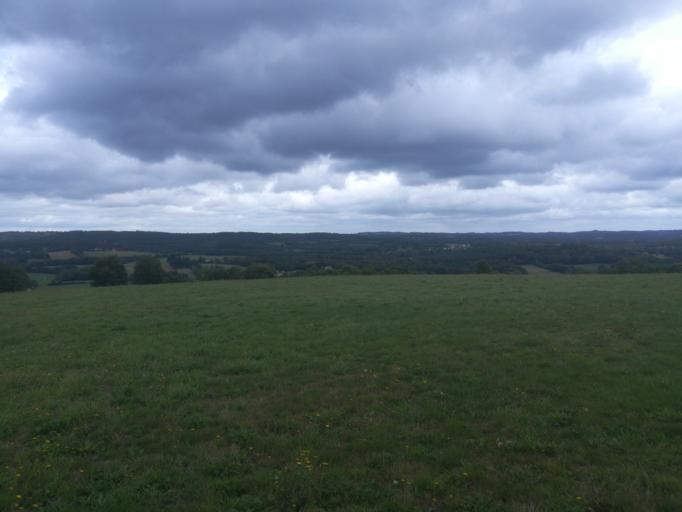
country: FR
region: Brittany
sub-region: Departement du Morbihan
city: Priziac
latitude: 48.0809
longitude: -3.3524
